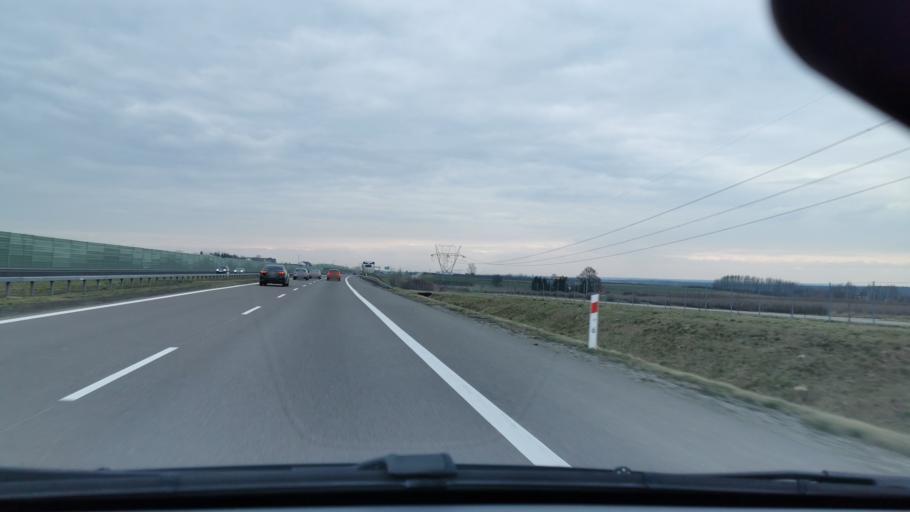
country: PL
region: Lublin Voivodeship
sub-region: Powiat lubelski
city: Garbow
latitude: 51.3774
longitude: 22.3085
